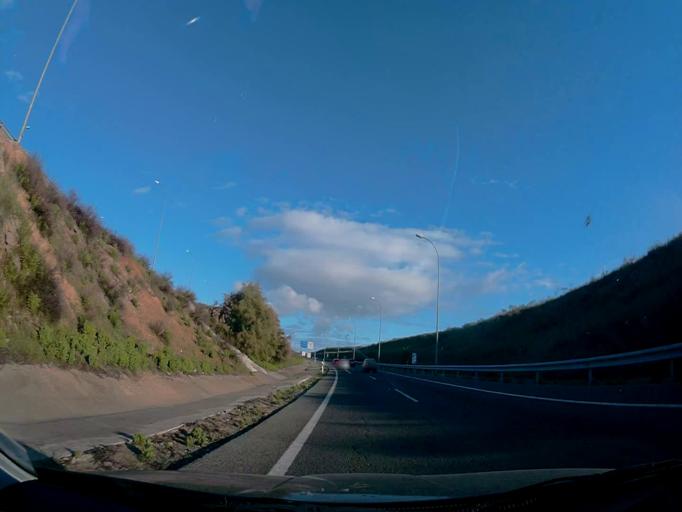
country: ES
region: Madrid
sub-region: Provincia de Madrid
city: Ajalvir
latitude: 40.5109
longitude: -3.4955
